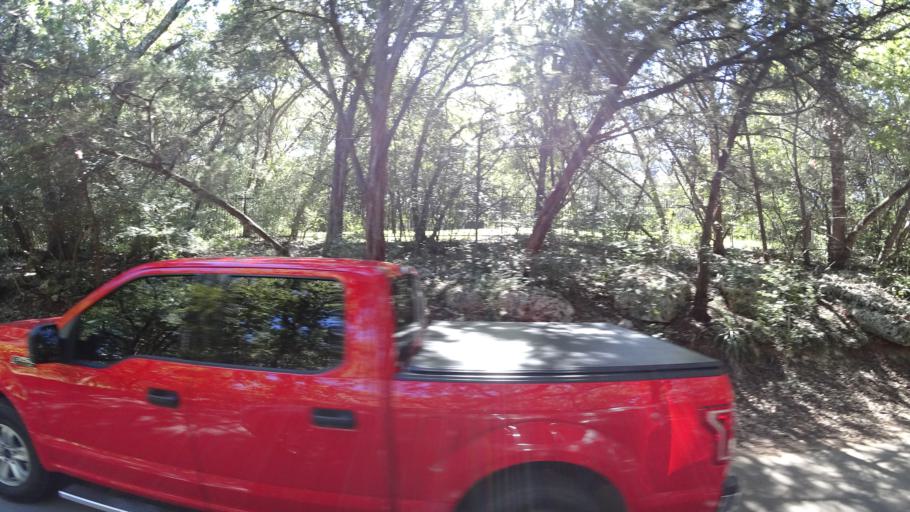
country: US
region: Texas
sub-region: Travis County
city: West Lake Hills
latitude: 30.3100
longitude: -97.7826
